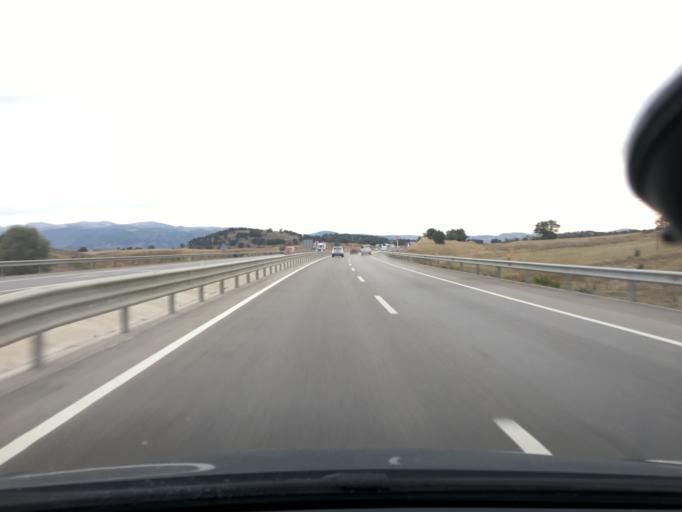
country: TR
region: Afyonkarahisar
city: Sincanli
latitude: 38.6582
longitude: 30.3223
